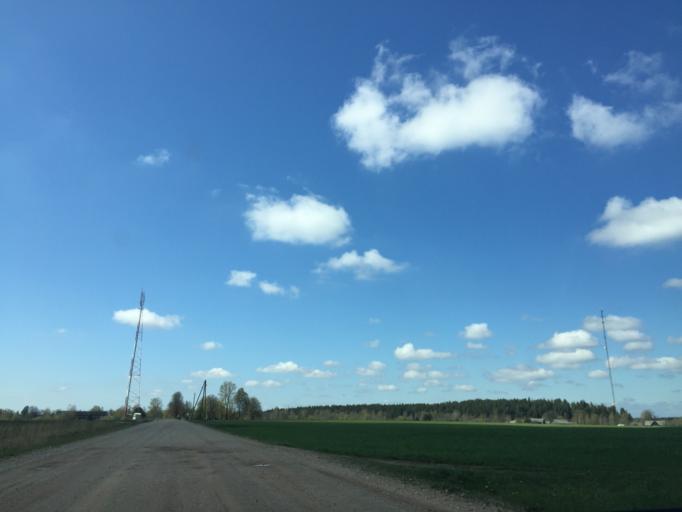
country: LV
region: Smiltene
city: Smiltene
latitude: 57.5850
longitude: 25.9717
